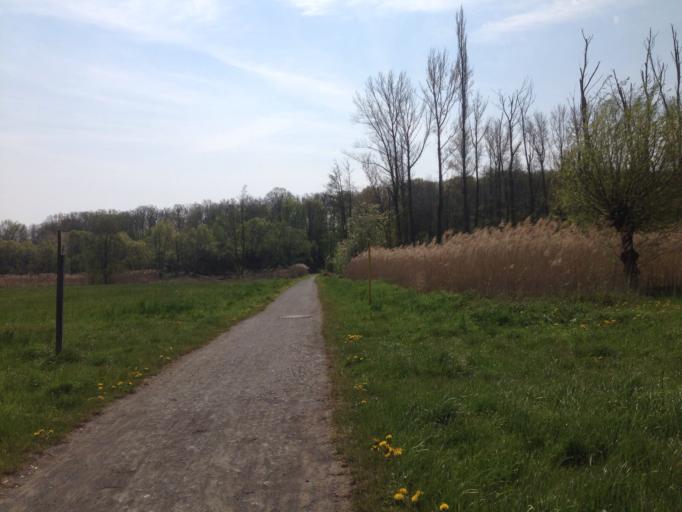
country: DE
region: Hesse
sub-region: Regierungsbezirk Giessen
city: Giessen
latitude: 50.5960
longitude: 8.6996
